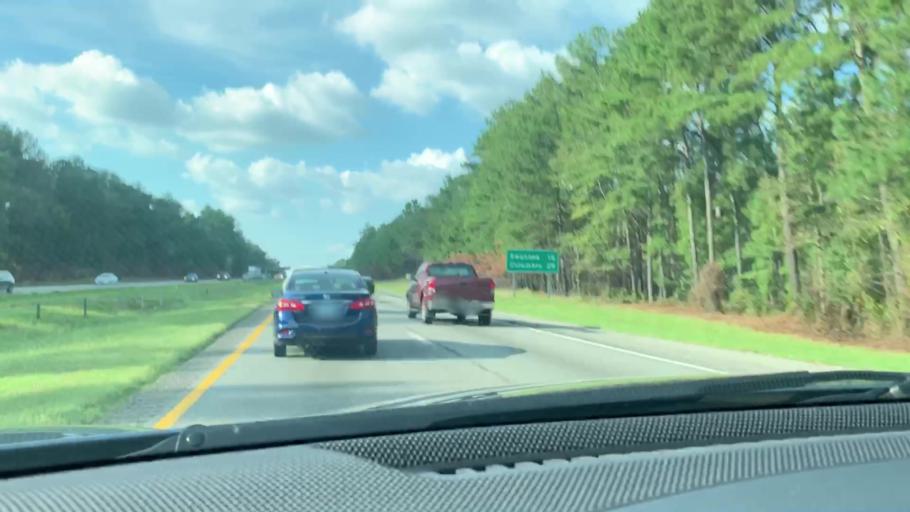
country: US
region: South Carolina
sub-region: Calhoun County
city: Saint Matthews
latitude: 33.6474
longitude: -80.8819
